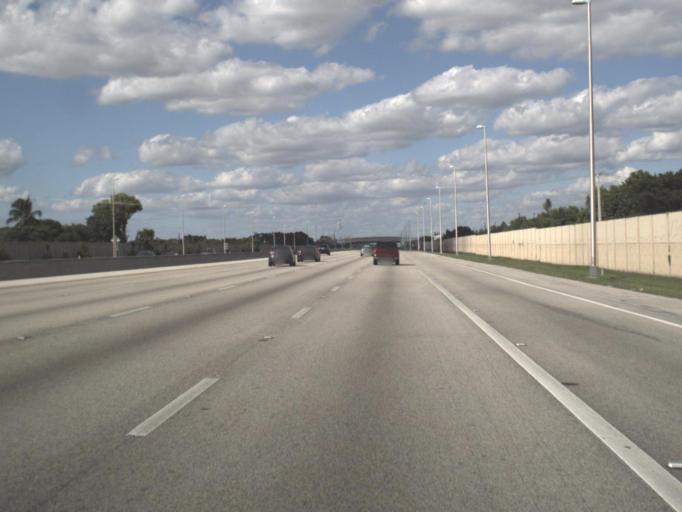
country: US
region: Florida
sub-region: Broward County
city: Lauderhill
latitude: 26.1418
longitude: -80.2191
